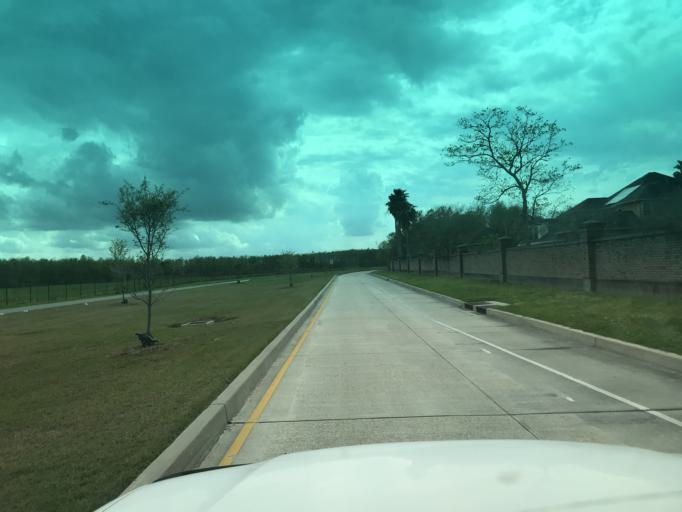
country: US
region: Louisiana
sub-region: Saint Bernard Parish
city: Chalmette
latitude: 30.0407
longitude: -89.9429
